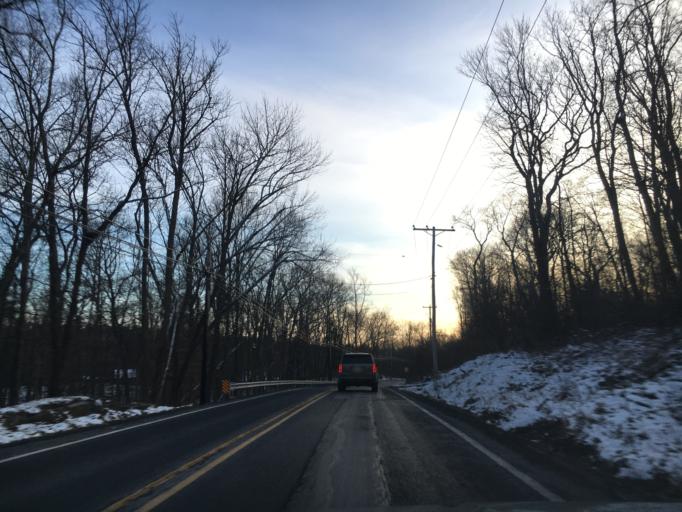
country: US
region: Pennsylvania
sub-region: Pike County
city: Saw Creek
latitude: 41.0963
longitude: -75.0991
